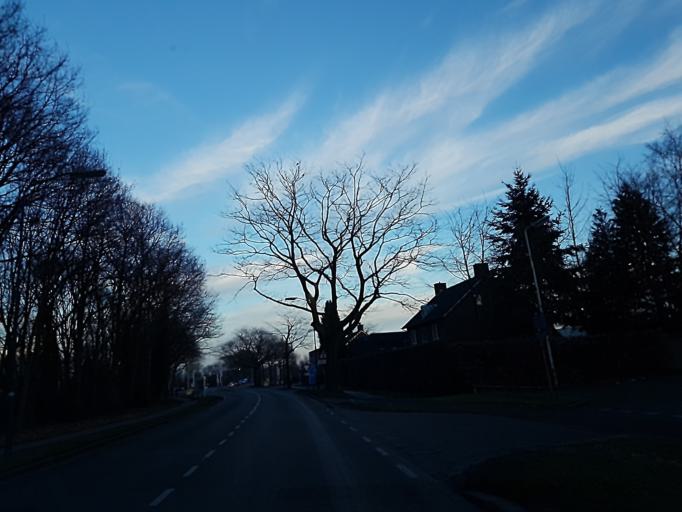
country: NL
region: North Brabant
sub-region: Gemeente Dongen
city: Dongen
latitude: 51.5442
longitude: 4.9510
